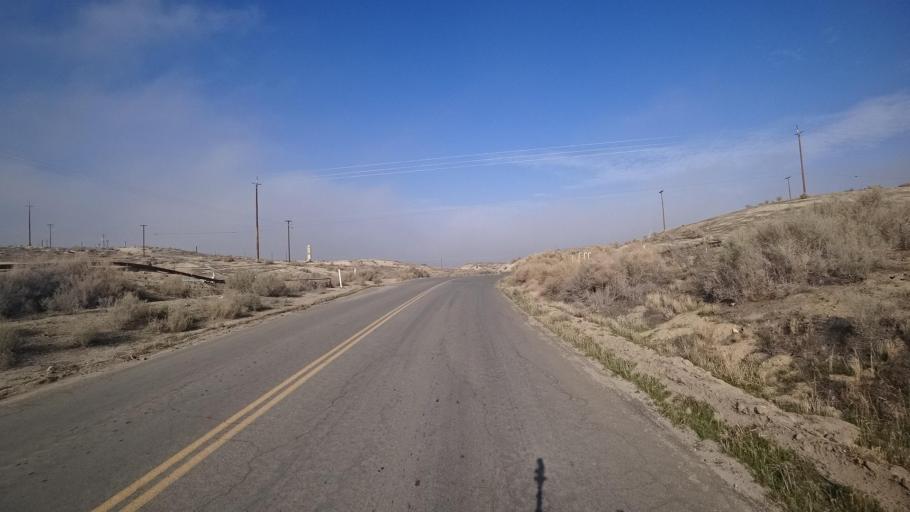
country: US
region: California
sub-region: Kern County
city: Ford City
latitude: 35.1641
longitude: -119.4209
